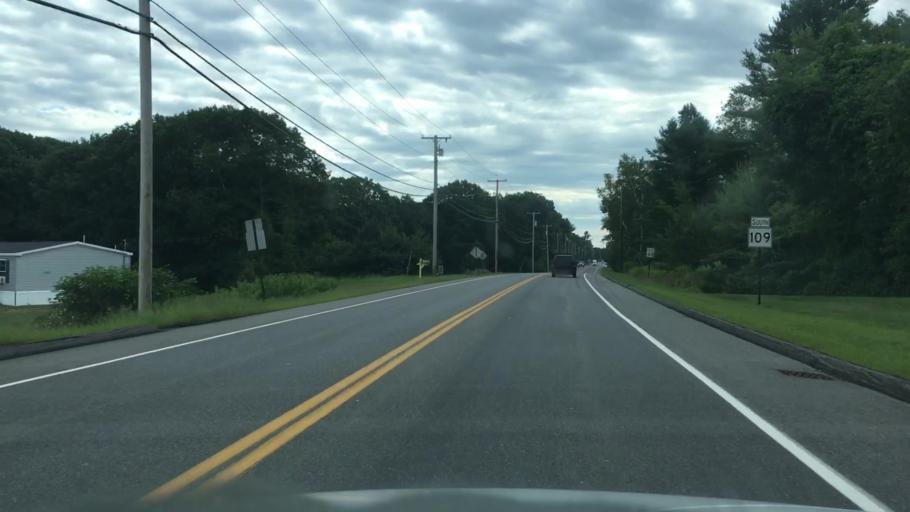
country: US
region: Maine
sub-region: York County
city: Wells Beach Station
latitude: 43.3315
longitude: -70.6247
